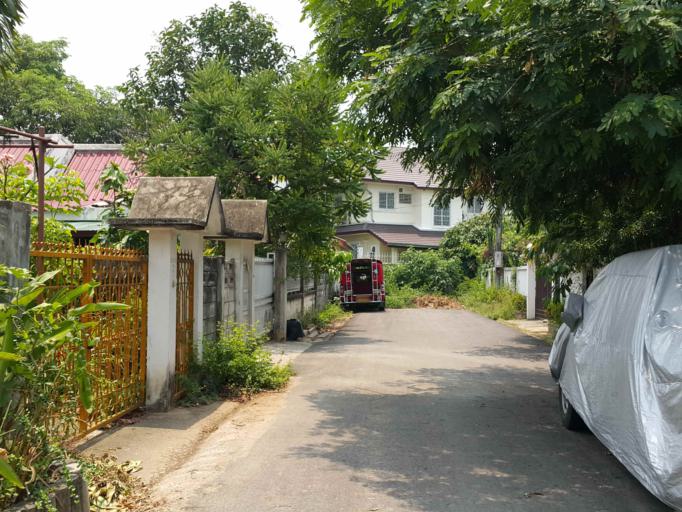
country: TH
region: Chiang Mai
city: Saraphi
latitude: 18.7533
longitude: 99.0123
